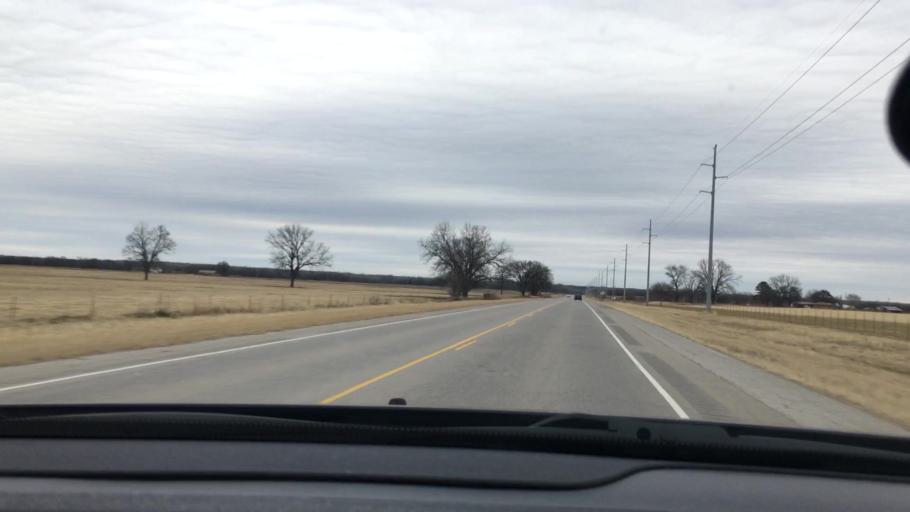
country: US
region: Oklahoma
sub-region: Marshall County
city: Oakland
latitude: 34.1959
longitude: -96.8022
